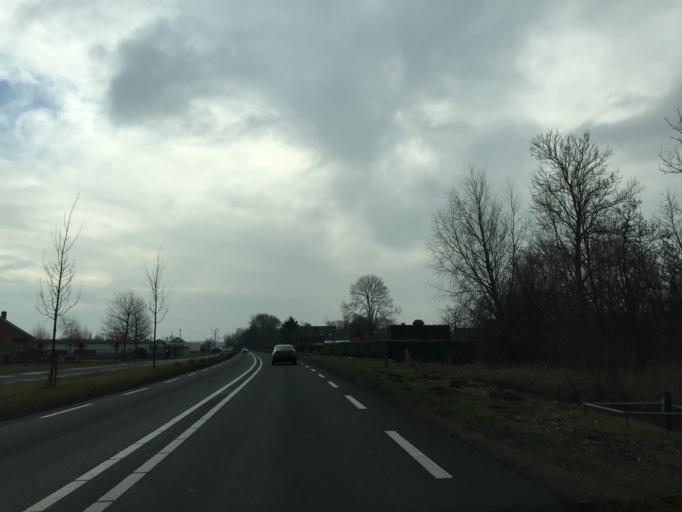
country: NL
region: South Holland
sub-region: Gemeente Capelle aan den IJssel
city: Capelle aan den IJssel
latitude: 51.9923
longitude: 4.5968
